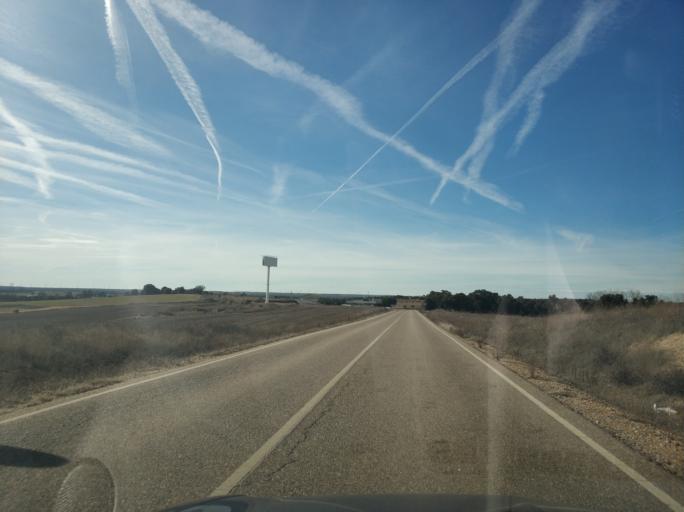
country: ES
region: Castille and Leon
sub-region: Provincia de Zamora
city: Cuelgamures
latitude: 41.2629
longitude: -5.7083
